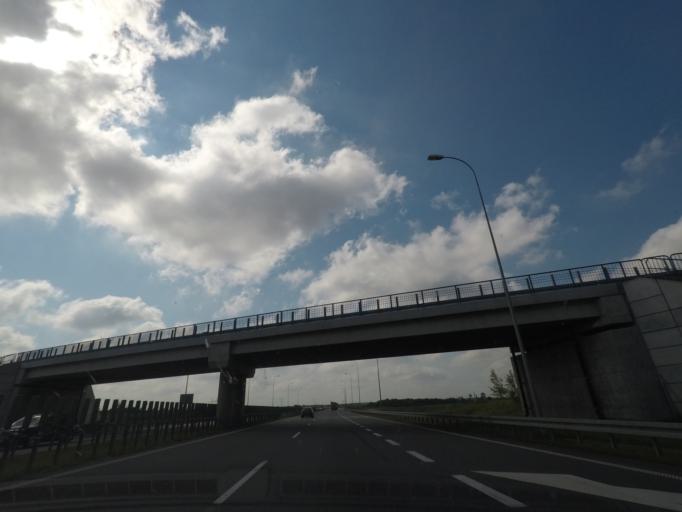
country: PL
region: Kujawsko-Pomorskie
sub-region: Powiat chelminski
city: Lisewo
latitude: 53.2555
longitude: 18.7252
